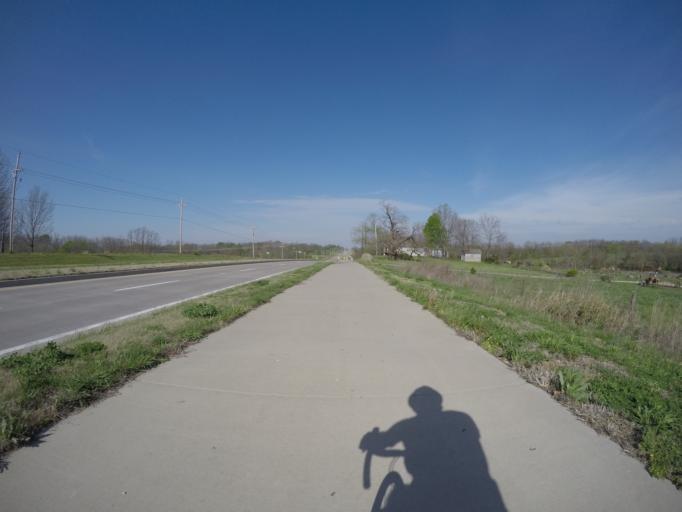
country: US
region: Missouri
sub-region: Cass County
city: Raymore
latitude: 38.8549
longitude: -94.4510
